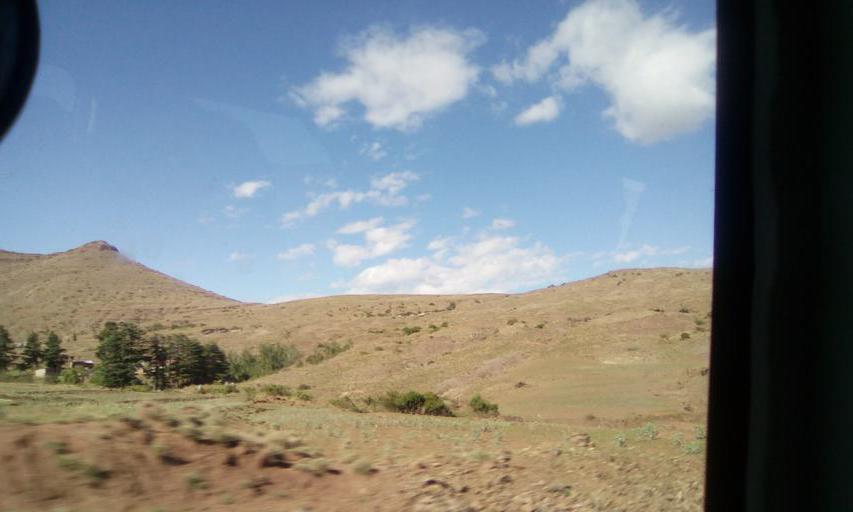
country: LS
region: Qacha's Nek
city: Qacha's Nek
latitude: -30.0431
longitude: 28.2684
